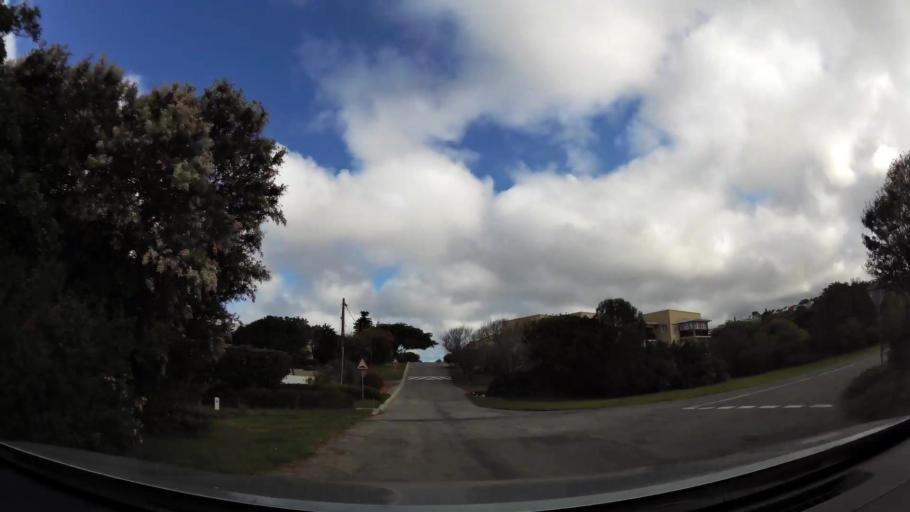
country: ZA
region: Western Cape
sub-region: Eden District Municipality
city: Plettenberg Bay
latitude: -34.0697
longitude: 23.3701
